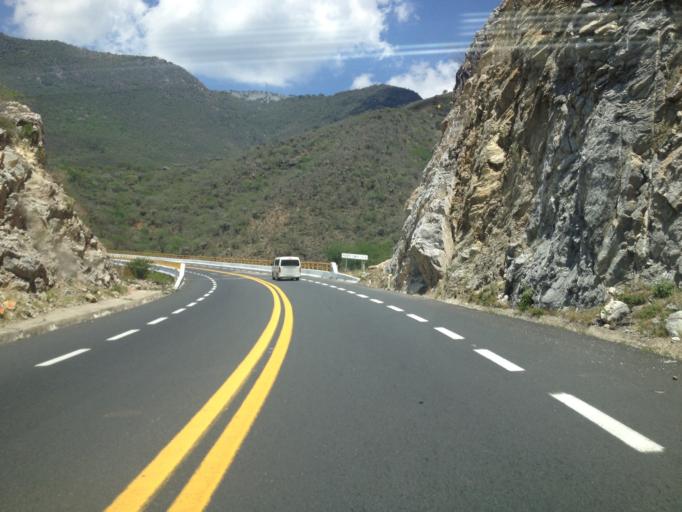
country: MX
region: Puebla
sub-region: San Jose Miahuatlan
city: San Pedro Tetitlan
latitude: 18.0903
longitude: -97.3417
